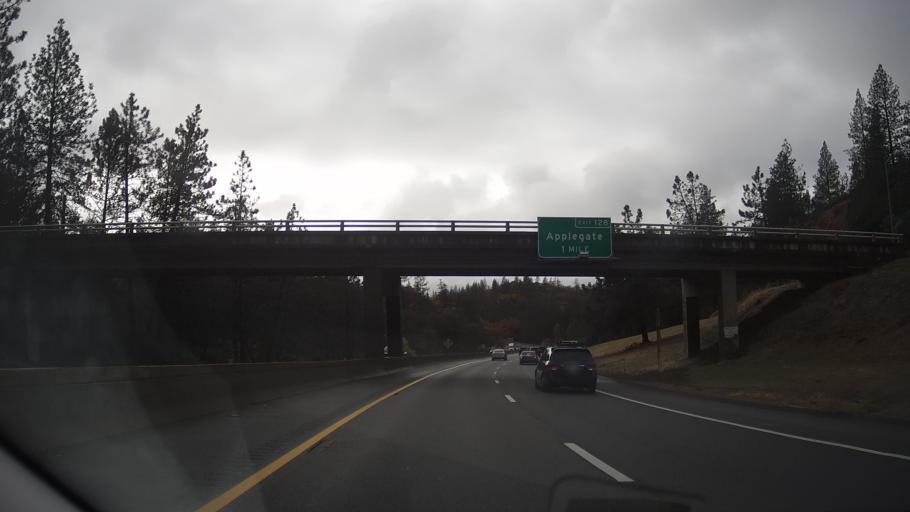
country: US
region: California
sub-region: Placer County
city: Meadow Vista
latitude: 39.0189
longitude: -120.9822
